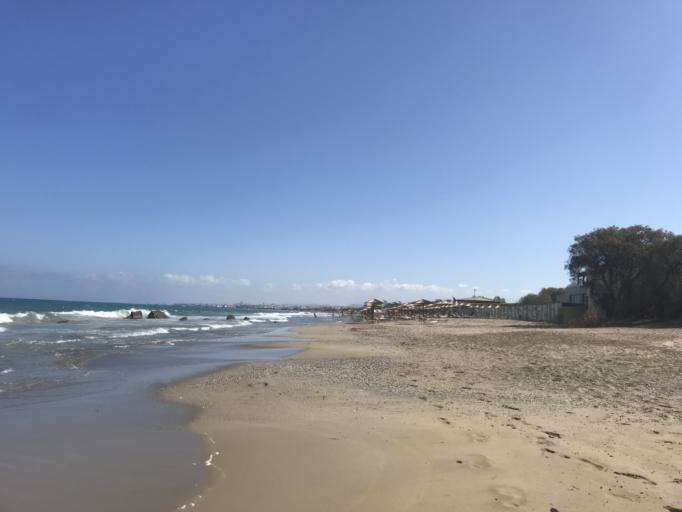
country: GR
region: Crete
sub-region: Nomos Irakleiou
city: Gazi
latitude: 35.3409
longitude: 25.0567
